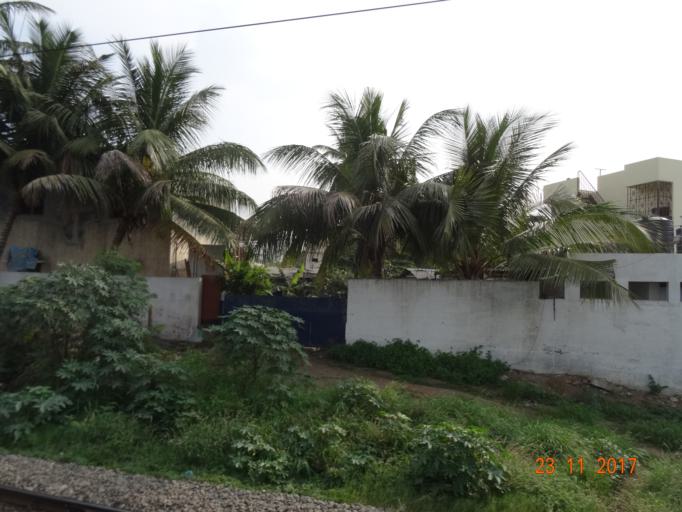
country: IN
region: Tamil Nadu
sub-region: Coimbatore
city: Coimbatore
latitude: 11.0283
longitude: 76.9724
